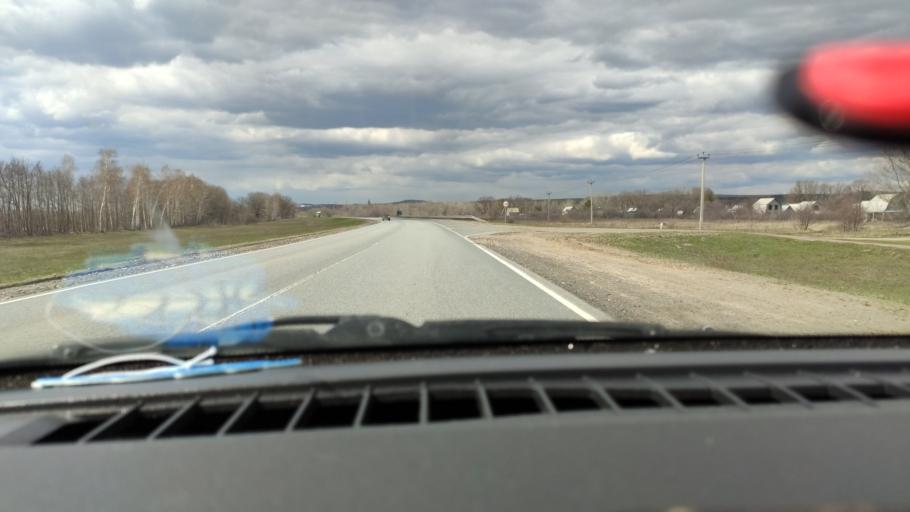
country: RU
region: Saratov
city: Tersa
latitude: 52.0858
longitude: 47.6012
